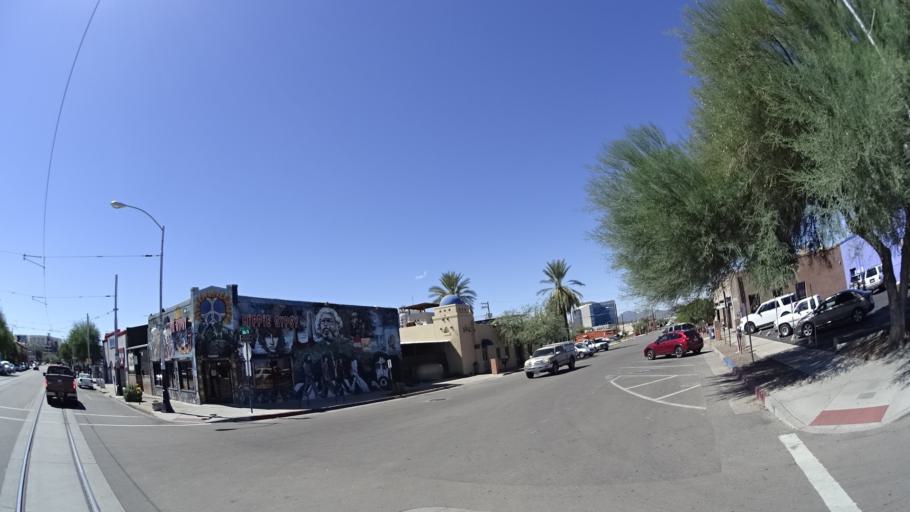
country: US
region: Arizona
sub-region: Pima County
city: South Tucson
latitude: 32.2266
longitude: -110.9656
